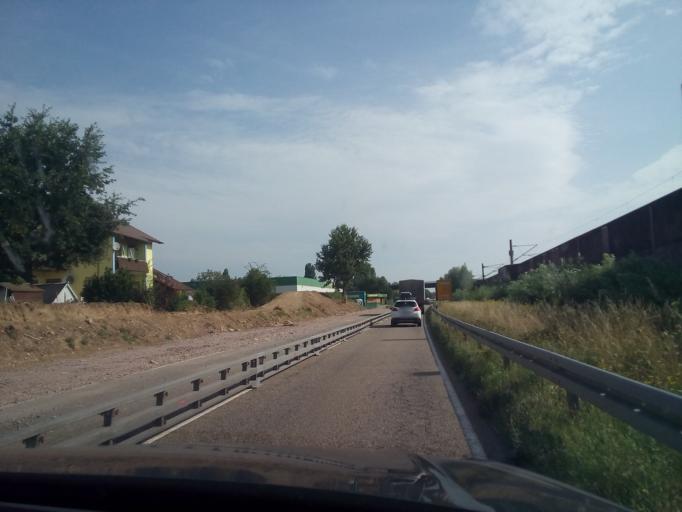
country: DE
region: Baden-Wuerttemberg
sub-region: Karlsruhe Region
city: Sinzheim
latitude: 48.7760
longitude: 8.1752
